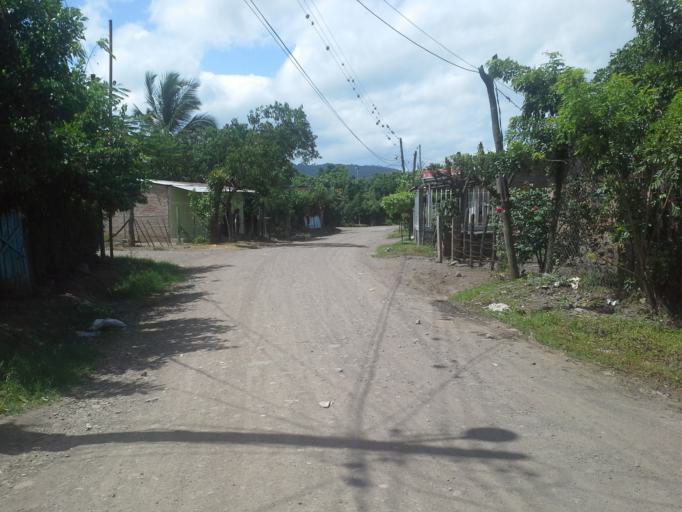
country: NI
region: Matagalpa
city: Ciudad Dario
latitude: 12.8591
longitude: -86.0981
